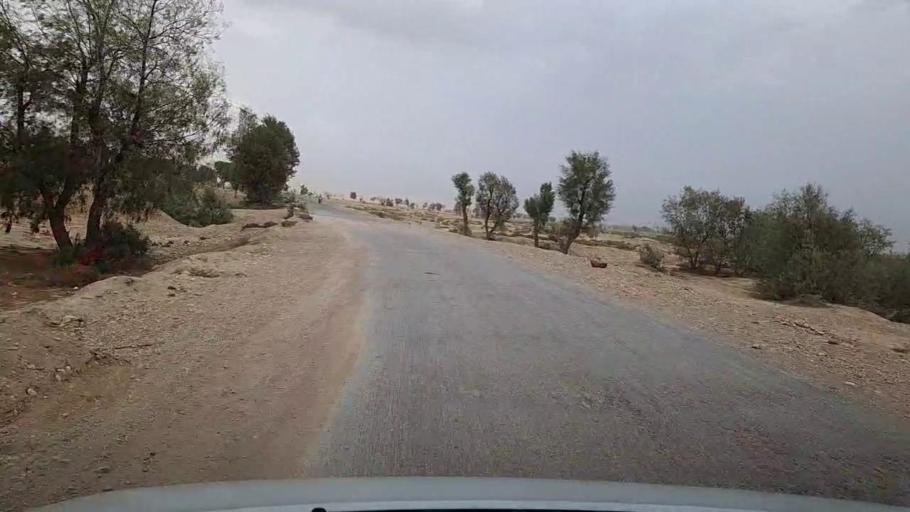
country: PK
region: Sindh
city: Sehwan
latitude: 26.3227
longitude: 67.7267
